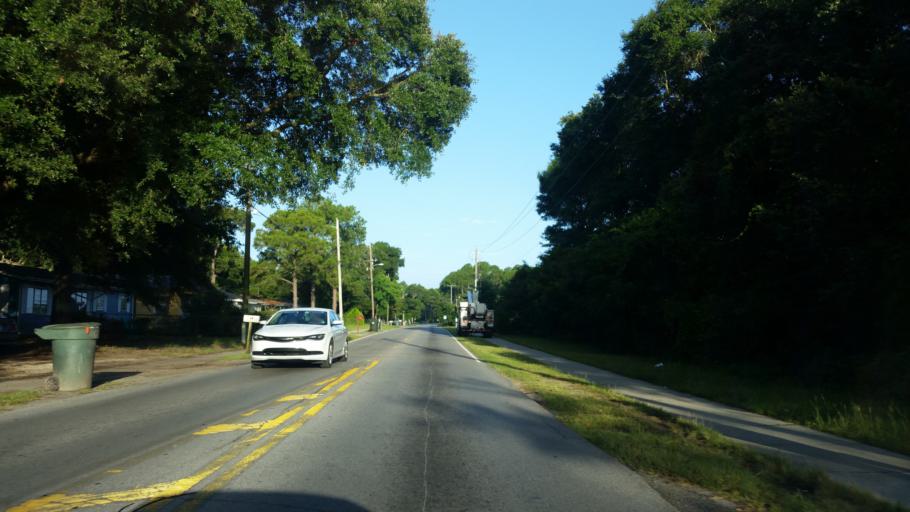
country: US
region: Florida
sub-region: Escambia County
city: Warrington
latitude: 30.3940
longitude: -87.2804
